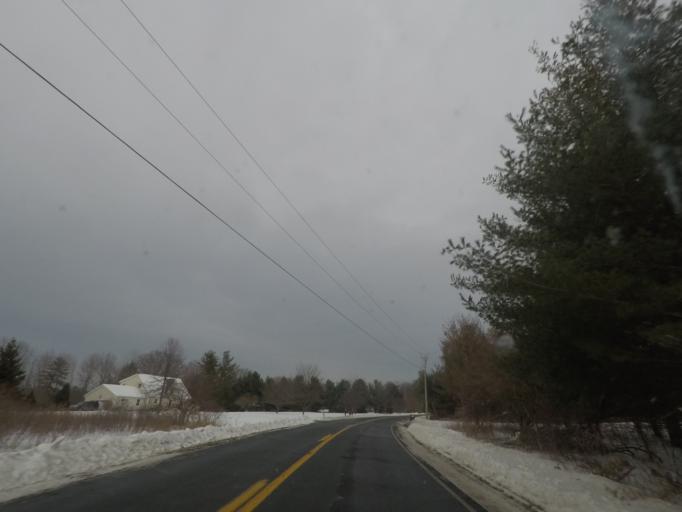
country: US
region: New York
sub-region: Rensselaer County
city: Castleton-on-Hudson
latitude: 42.5173
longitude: -73.7349
